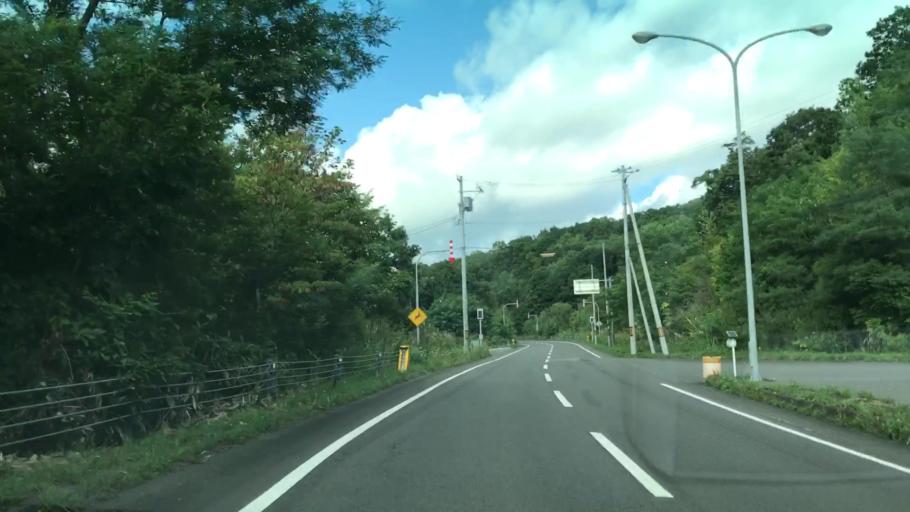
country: JP
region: Hokkaido
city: Muroran
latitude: 42.3685
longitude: 140.9558
